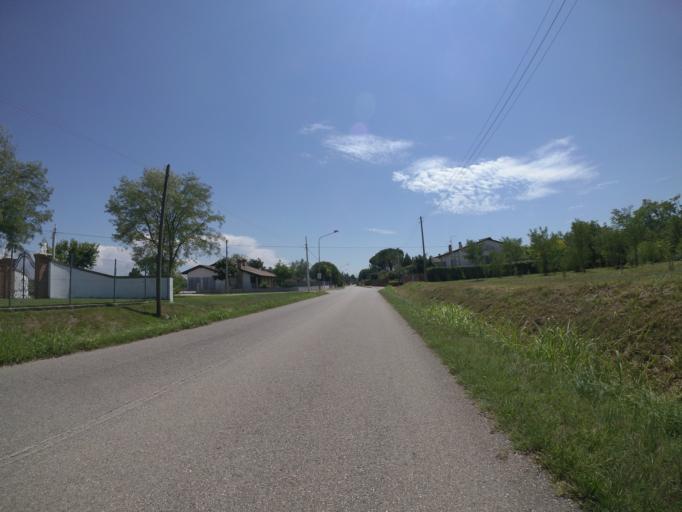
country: IT
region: Friuli Venezia Giulia
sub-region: Provincia di Udine
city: Talmassons
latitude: 45.9357
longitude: 13.1154
